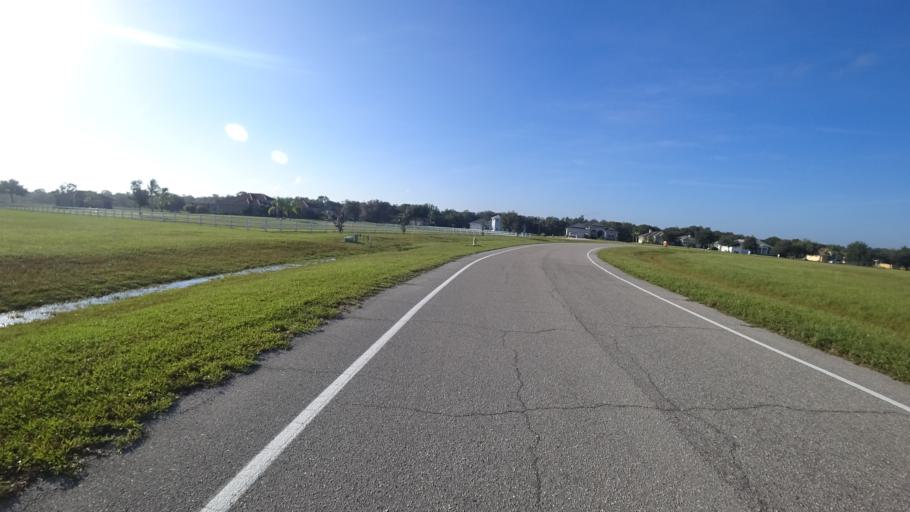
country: US
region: Florida
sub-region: Hillsborough County
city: Sun City Center
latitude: 27.5630
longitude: -82.3533
